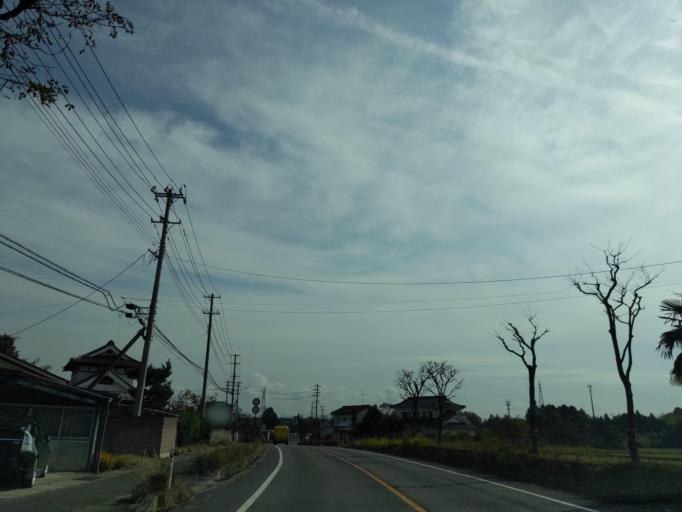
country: JP
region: Fukushima
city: Koriyama
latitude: 37.4177
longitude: 140.3243
